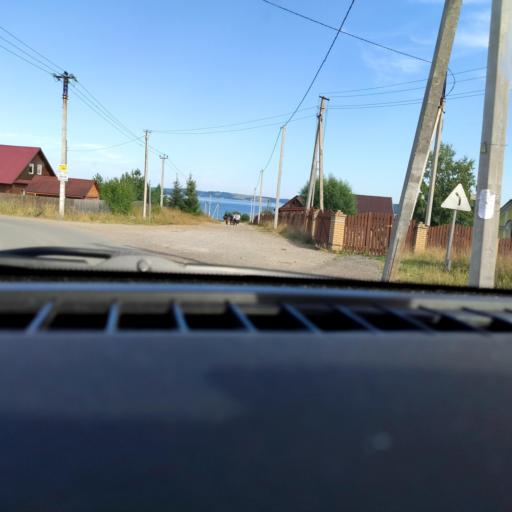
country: RU
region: Perm
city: Polazna
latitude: 58.3453
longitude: 56.2470
